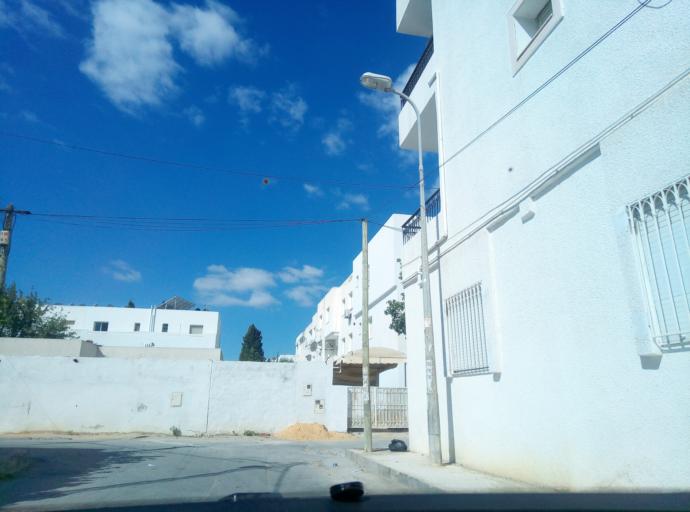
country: TN
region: Tunis
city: La Goulette
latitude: 36.8541
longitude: 10.2624
